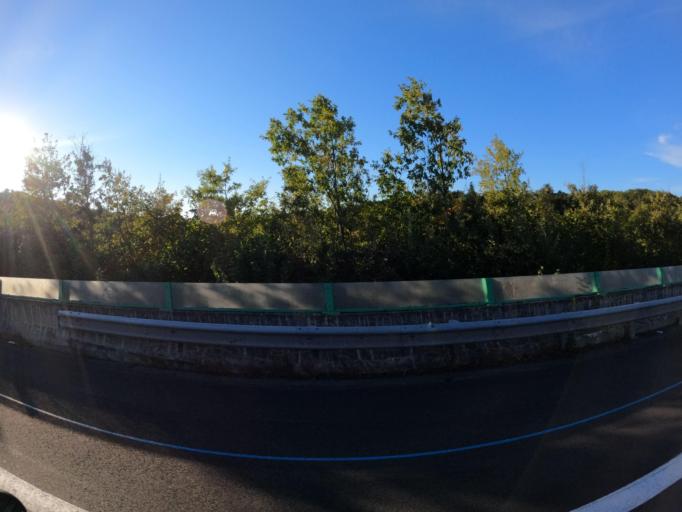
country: FR
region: Pays de la Loire
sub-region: Departement de la Vendee
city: Saint-Laurent-sur-Sevre
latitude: 46.9650
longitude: -0.9222
